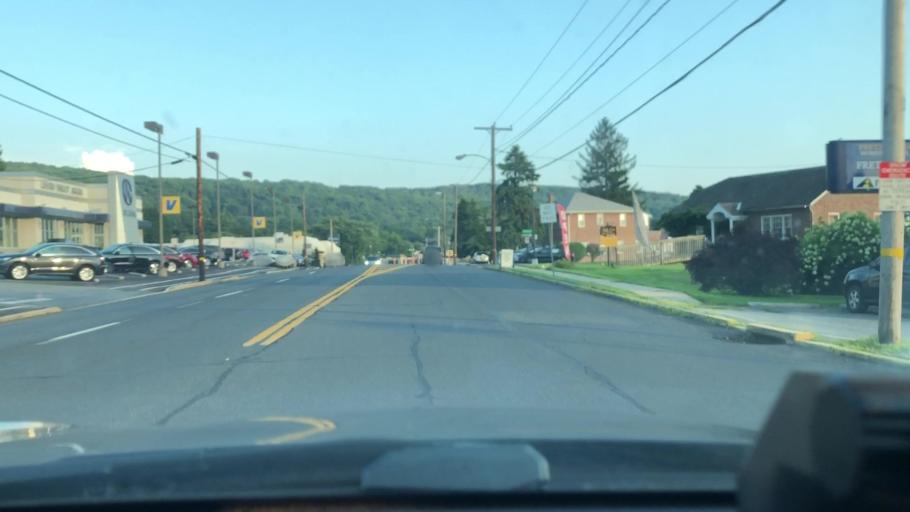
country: US
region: Pennsylvania
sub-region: Lehigh County
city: Emmaus
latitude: 40.5460
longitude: -75.4885
